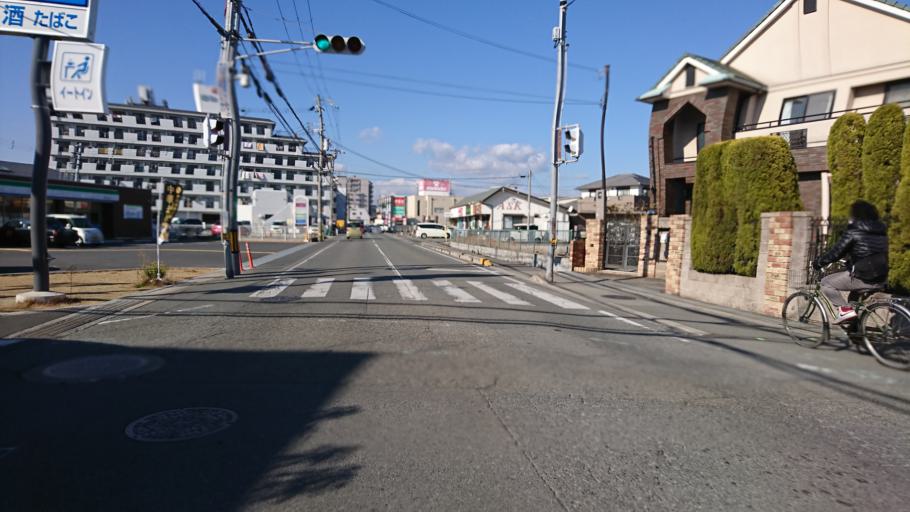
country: JP
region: Hyogo
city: Kakogawacho-honmachi
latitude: 34.7376
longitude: 134.8632
